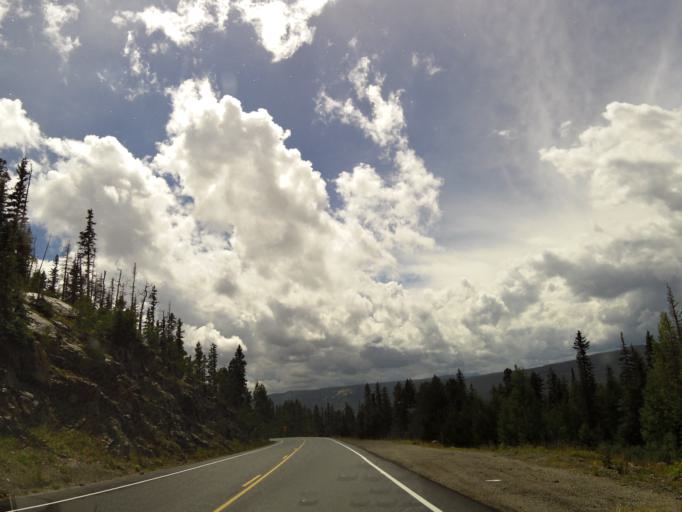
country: US
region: Colorado
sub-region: San Juan County
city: Silverton
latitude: 37.6794
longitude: -107.7797
